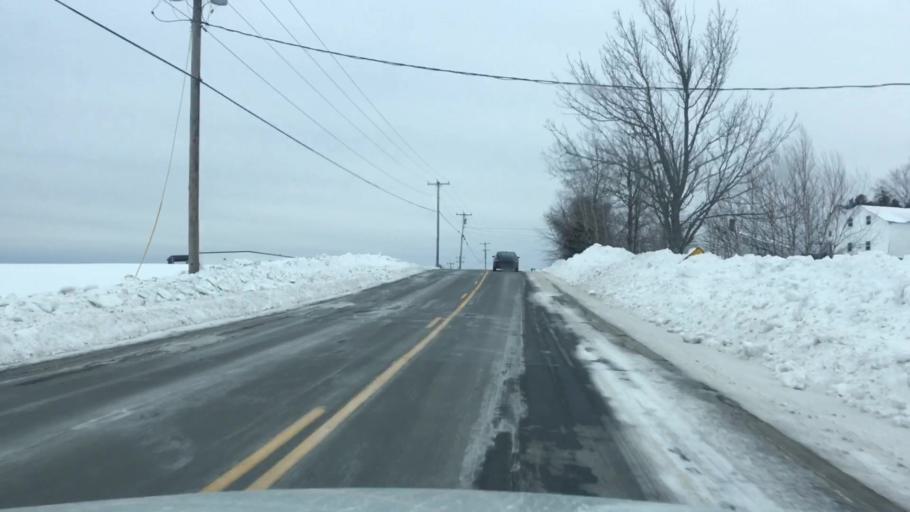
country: US
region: Maine
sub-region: Penobscot County
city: Garland
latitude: 44.9785
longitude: -69.0898
